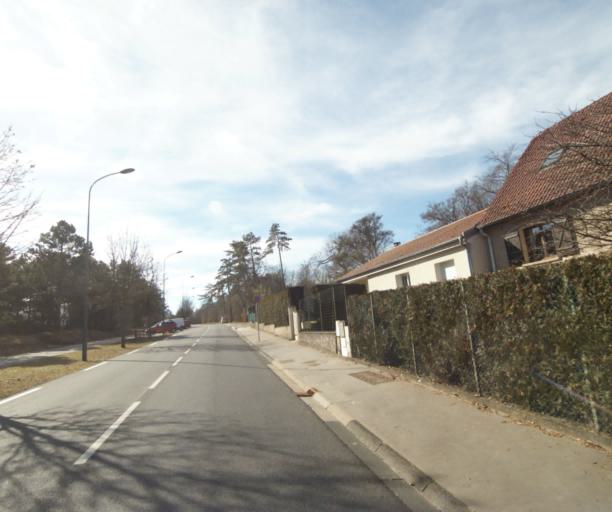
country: FR
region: Lorraine
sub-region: Departement de Meurthe-et-Moselle
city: Villers-les-Nancy
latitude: 48.6632
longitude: 6.1336
